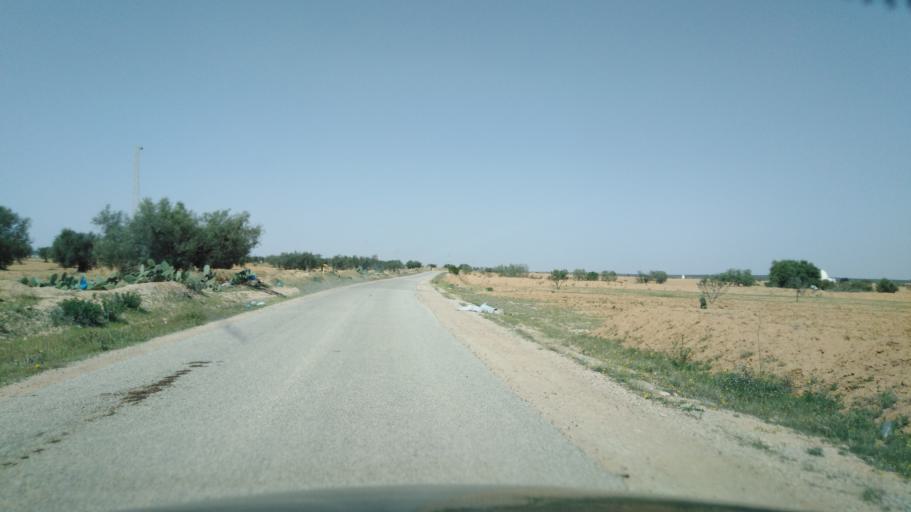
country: TN
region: Safaqis
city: Sfax
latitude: 34.6757
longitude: 10.4444
